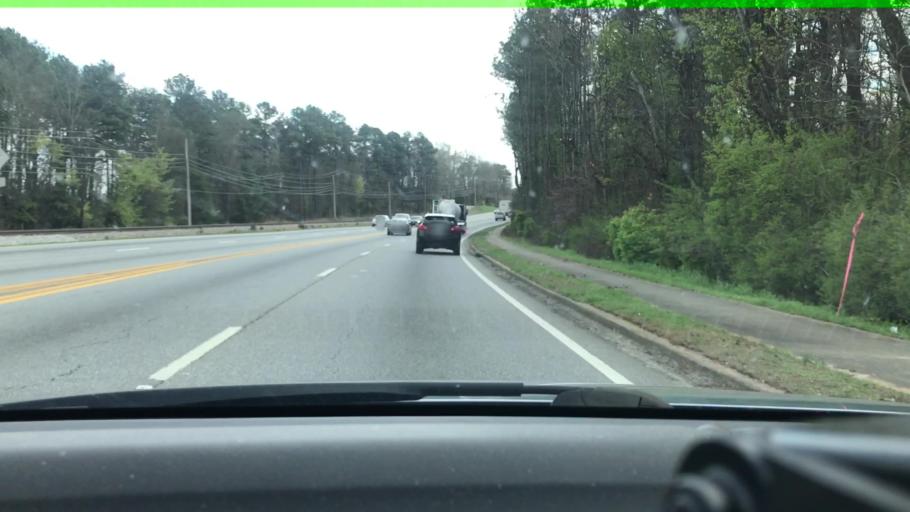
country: US
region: Georgia
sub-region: Clarke County
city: Country Club Estates
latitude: 33.9822
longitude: -83.4166
